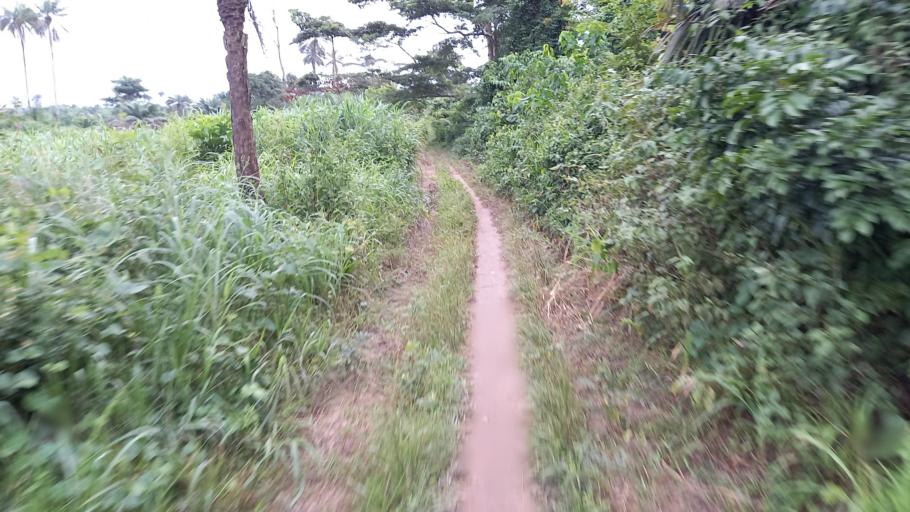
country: SL
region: Eastern Province
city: Kailahun
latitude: 8.2919
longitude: -10.5694
